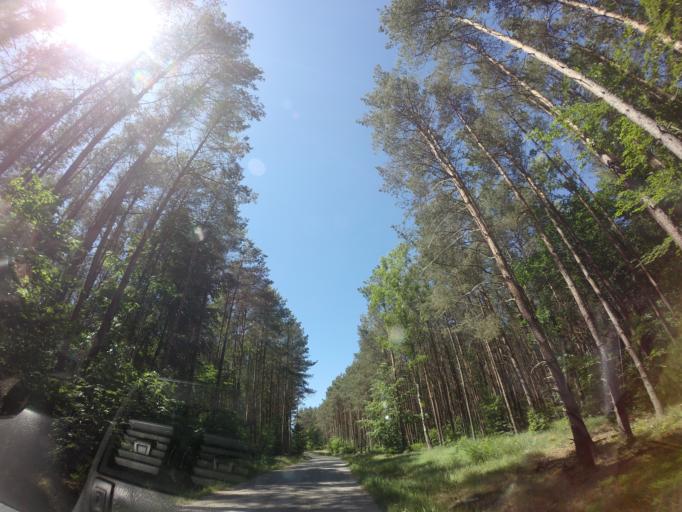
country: PL
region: Lubusz
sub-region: Powiat strzelecko-drezdenecki
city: Dobiegniew
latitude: 53.0745
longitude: 15.8424
